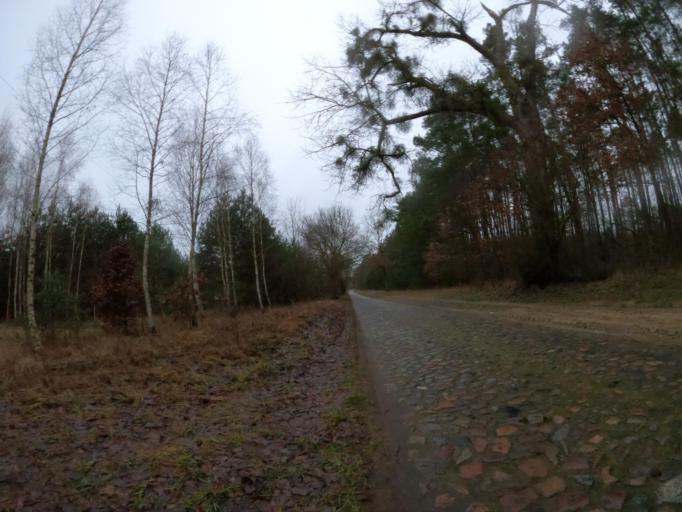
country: PL
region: West Pomeranian Voivodeship
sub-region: Powiat mysliborski
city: Debno
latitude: 52.8089
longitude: 14.7369
